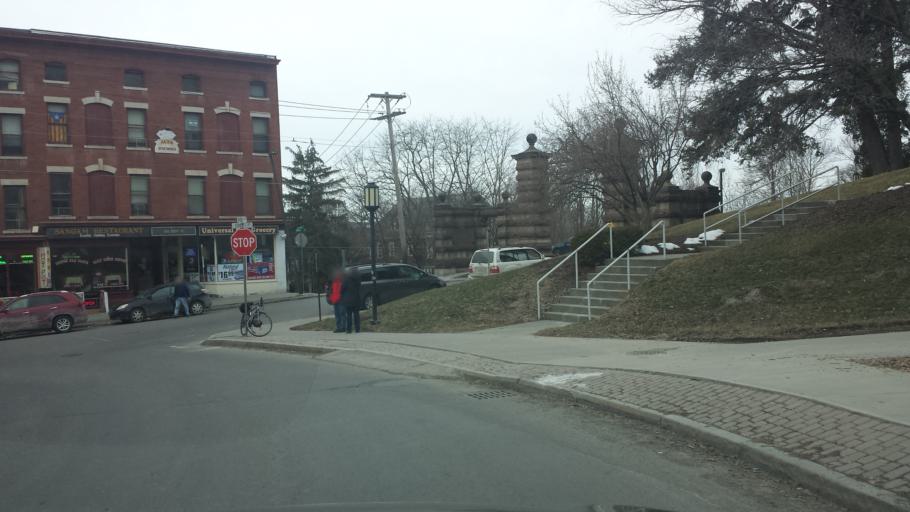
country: US
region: New York
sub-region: Tompkins County
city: East Ithaca
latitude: 42.4421
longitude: -76.4871
